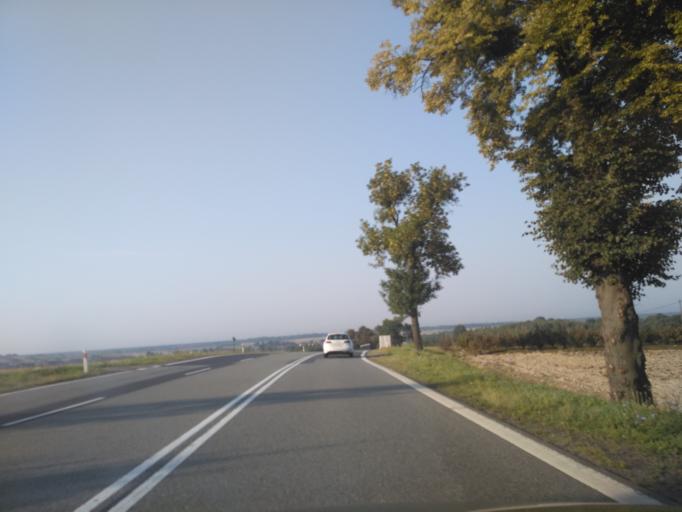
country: PL
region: Lublin Voivodeship
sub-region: Powiat janowski
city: Modliborzyce
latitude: 50.7671
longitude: 22.3245
